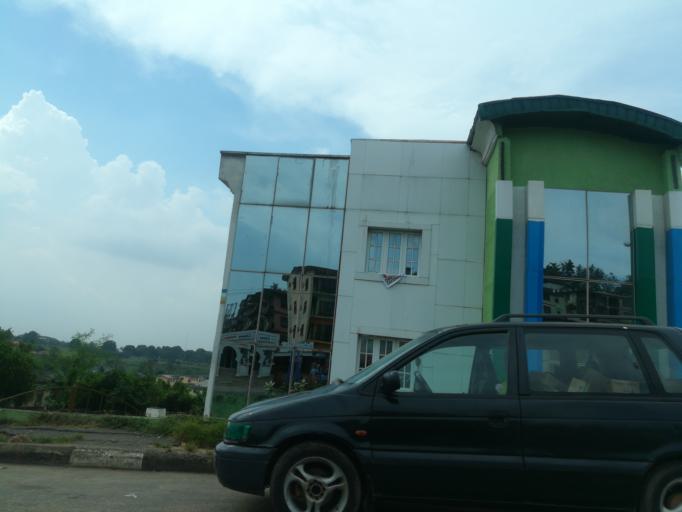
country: NG
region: Oyo
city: Ibadan
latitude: 7.4104
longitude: 3.8916
